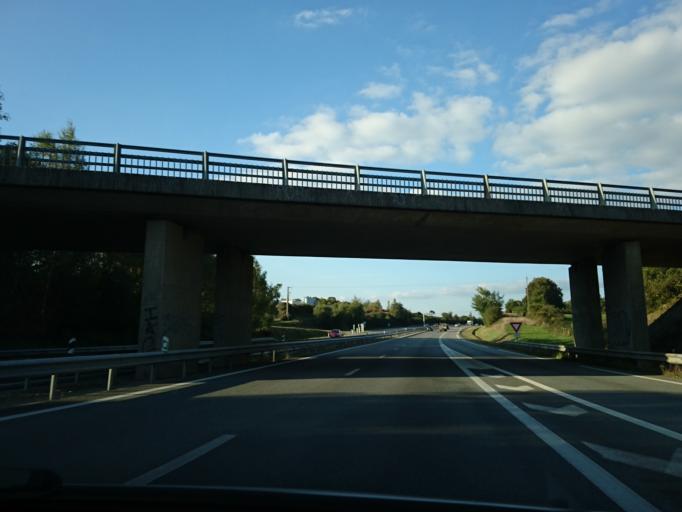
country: FR
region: Brittany
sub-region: Departement d'Ille-et-Vilaine
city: Grand-Fougeray
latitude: 47.7453
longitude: -1.7154
